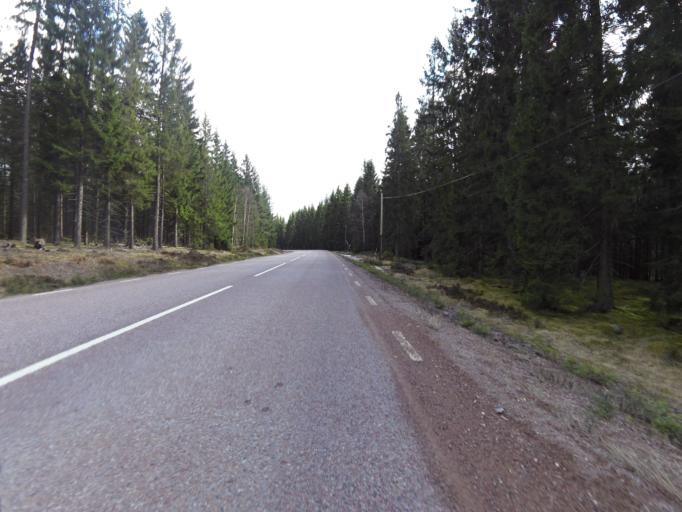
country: SE
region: Dalarna
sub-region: Avesta Kommun
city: Horndal
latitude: 60.3066
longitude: 16.2472
